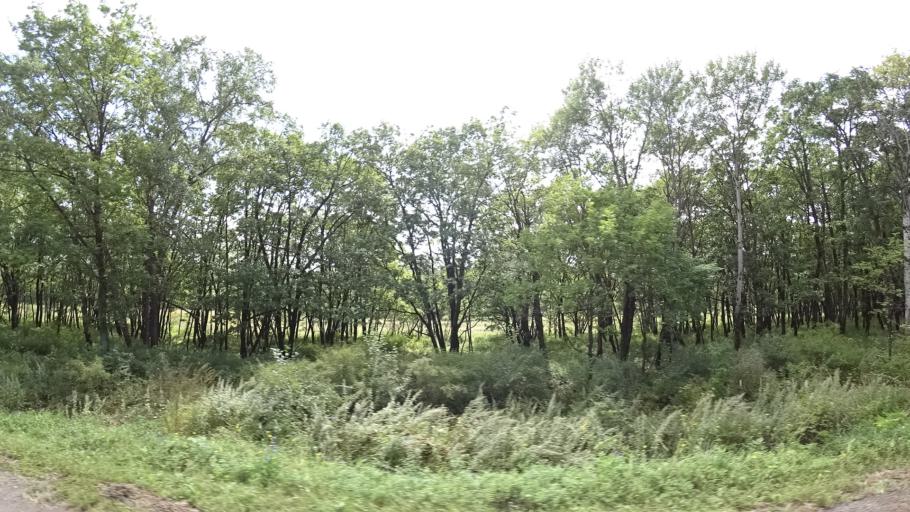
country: RU
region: Primorskiy
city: Lyalichi
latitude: 44.1410
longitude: 132.4089
